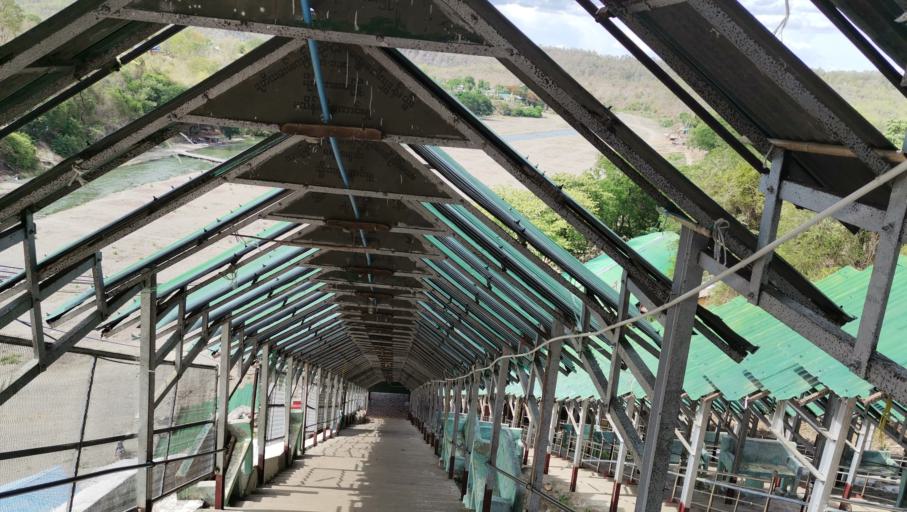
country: MM
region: Magway
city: Minbu
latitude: 20.1016
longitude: 94.5273
